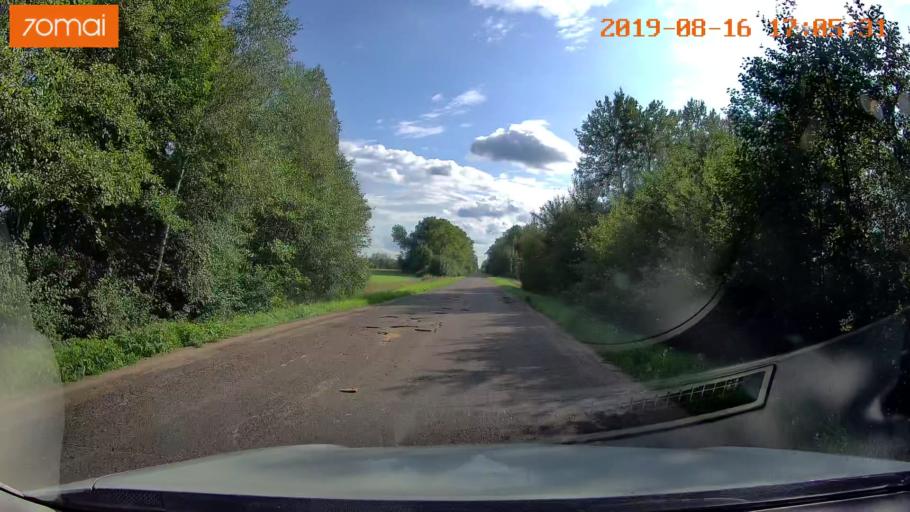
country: BY
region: Mogilev
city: Hlusha
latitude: 53.2366
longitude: 28.9433
